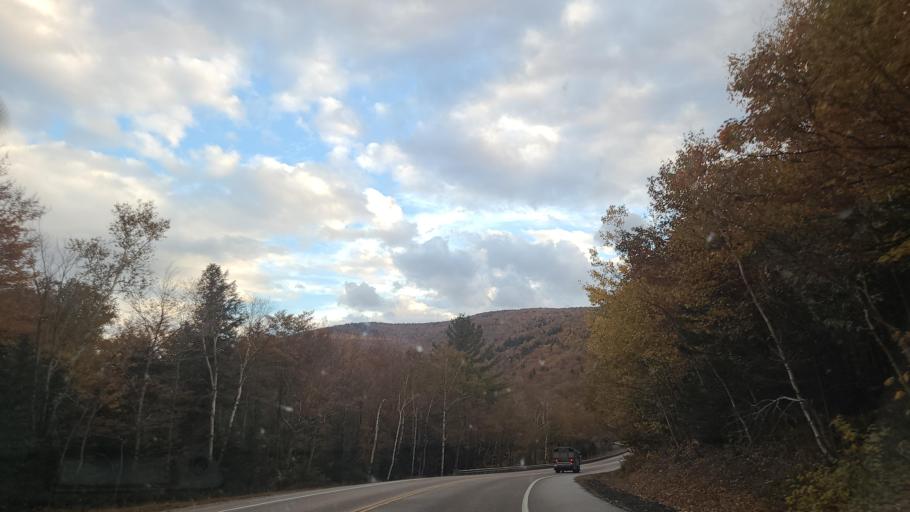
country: US
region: New Hampshire
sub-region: Grafton County
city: Deerfield
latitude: 44.1764
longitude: -71.3943
